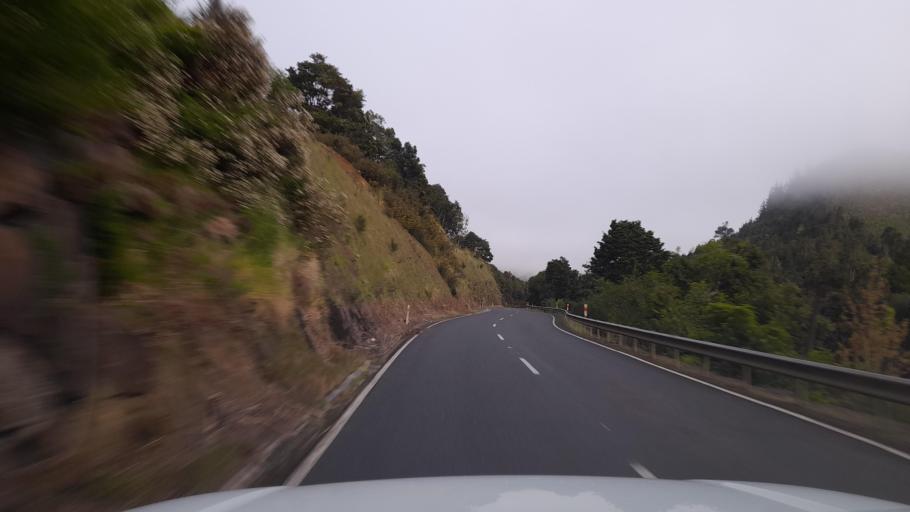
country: NZ
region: Northland
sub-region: Far North District
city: Moerewa
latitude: -35.6284
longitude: 173.8515
